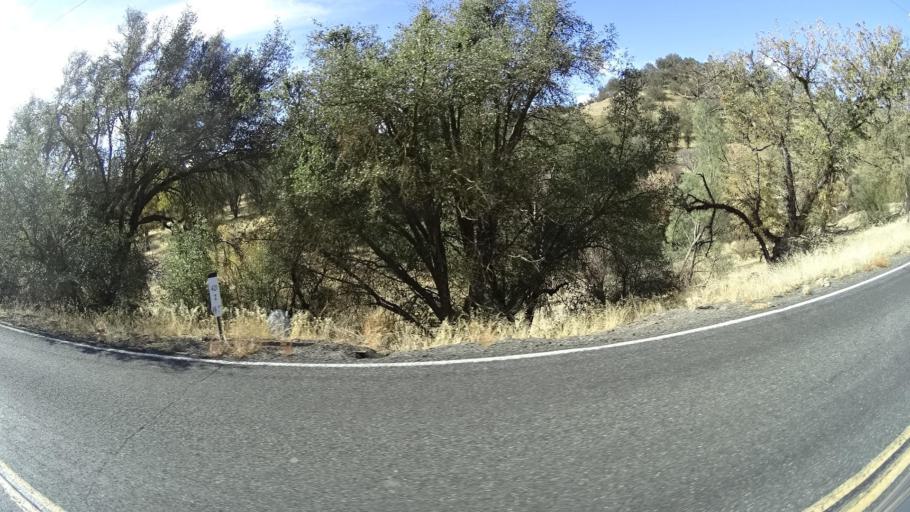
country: US
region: California
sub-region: Kern County
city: Alta Sierra
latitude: 35.6895
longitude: -118.7311
